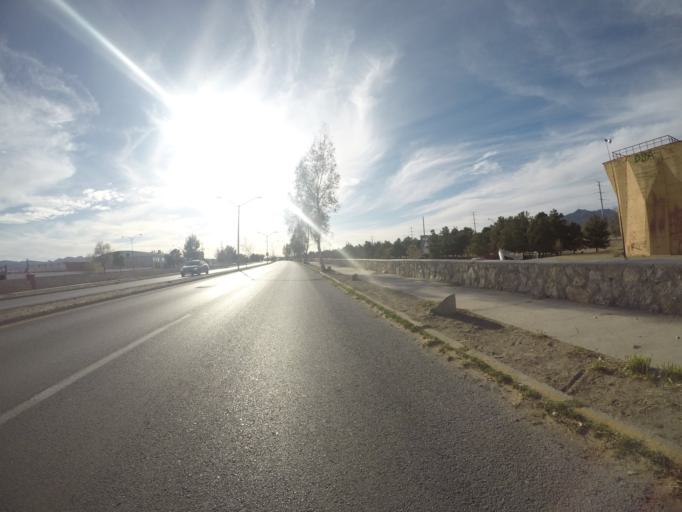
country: US
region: Texas
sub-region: El Paso County
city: El Paso
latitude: 31.7545
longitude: -106.4439
